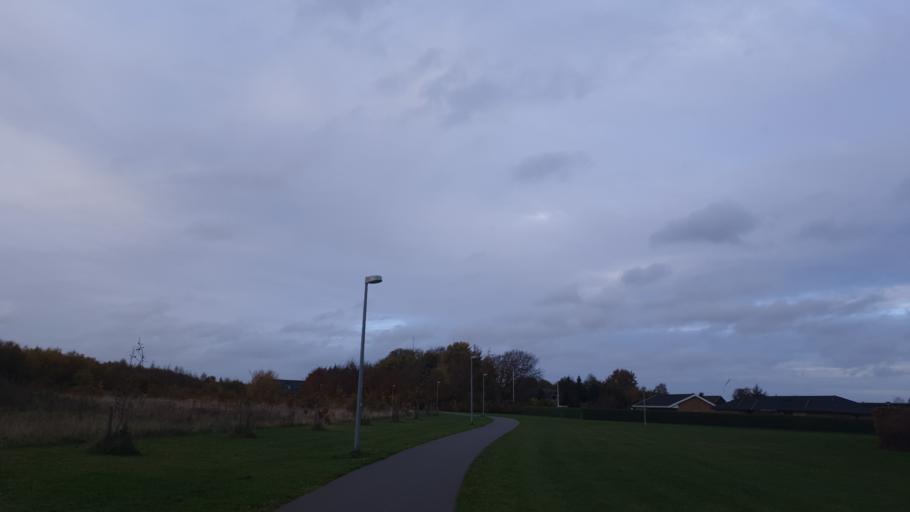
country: DK
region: Central Jutland
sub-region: Hedensted Kommune
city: Hedensted
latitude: 55.7885
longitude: 9.6923
